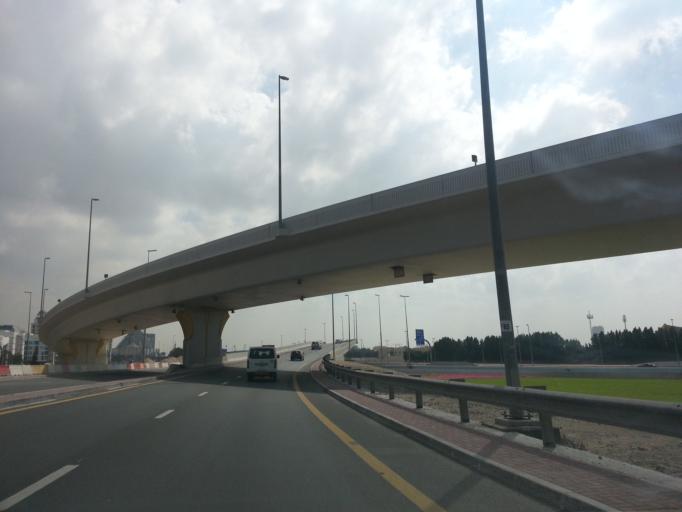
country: AE
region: Ash Shariqah
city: Sharjah
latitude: 25.2339
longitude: 55.3058
